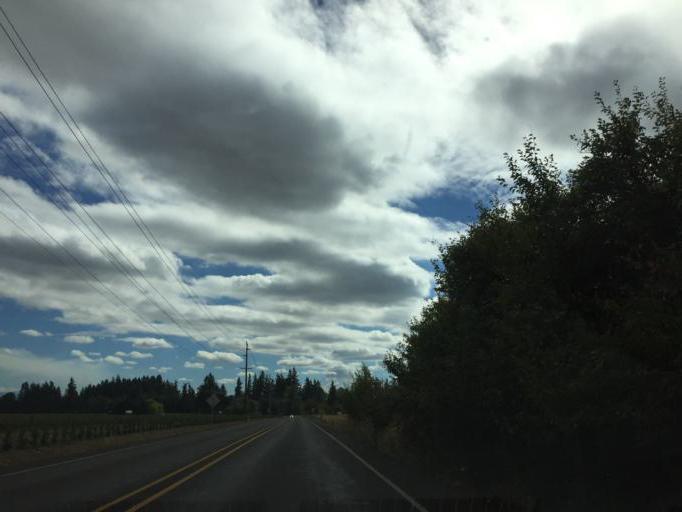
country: US
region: Oregon
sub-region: Marion County
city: Woodburn
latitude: 45.1349
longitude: -122.8345
